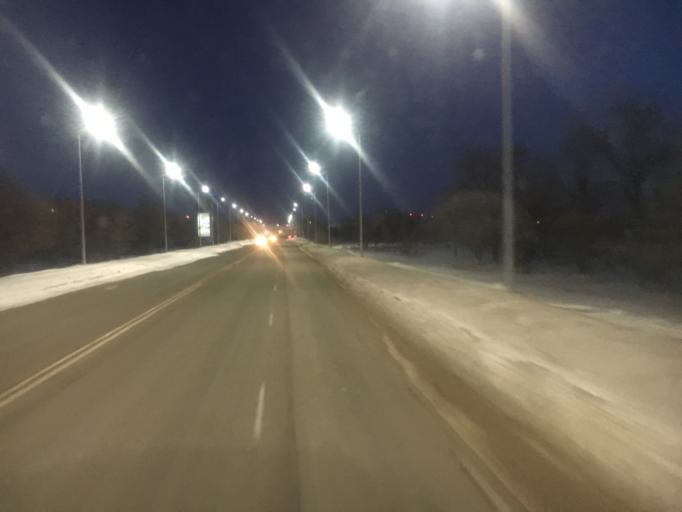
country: KZ
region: Batys Qazaqstan
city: Oral
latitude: 51.1571
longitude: 51.5341
